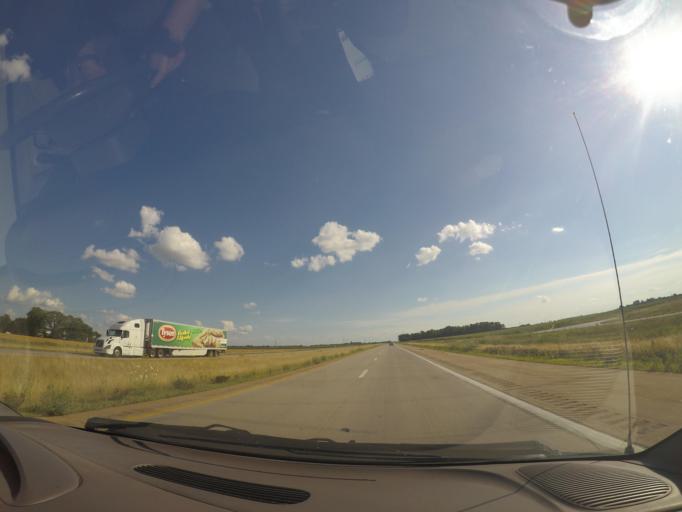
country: US
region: Ohio
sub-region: Lucas County
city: Whitehouse
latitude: 41.4892
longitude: -83.7702
